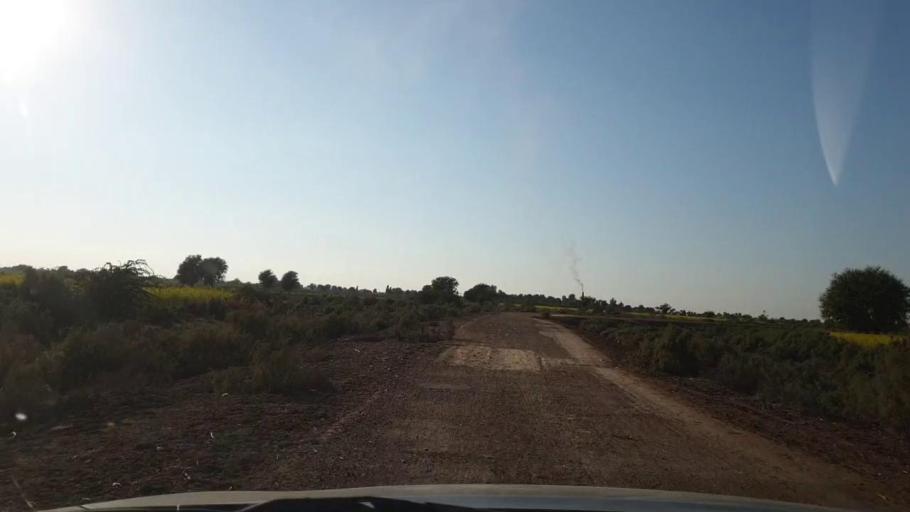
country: PK
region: Sindh
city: Jhol
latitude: 25.8981
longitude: 68.9289
